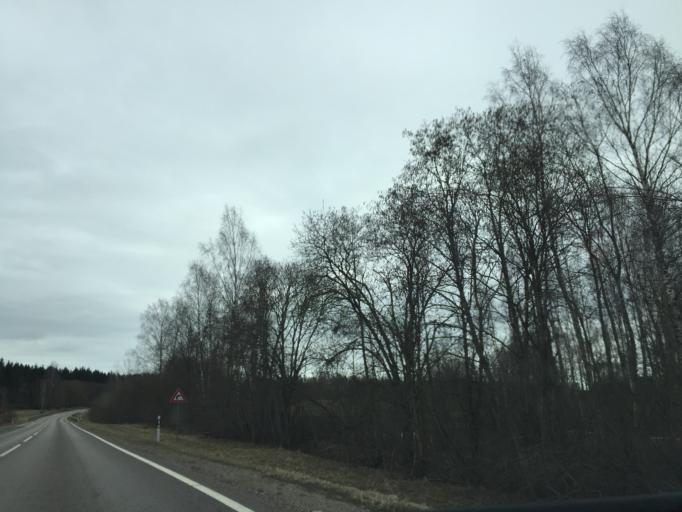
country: LV
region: Kraslavas Rajons
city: Kraslava
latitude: 55.9100
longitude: 27.0881
